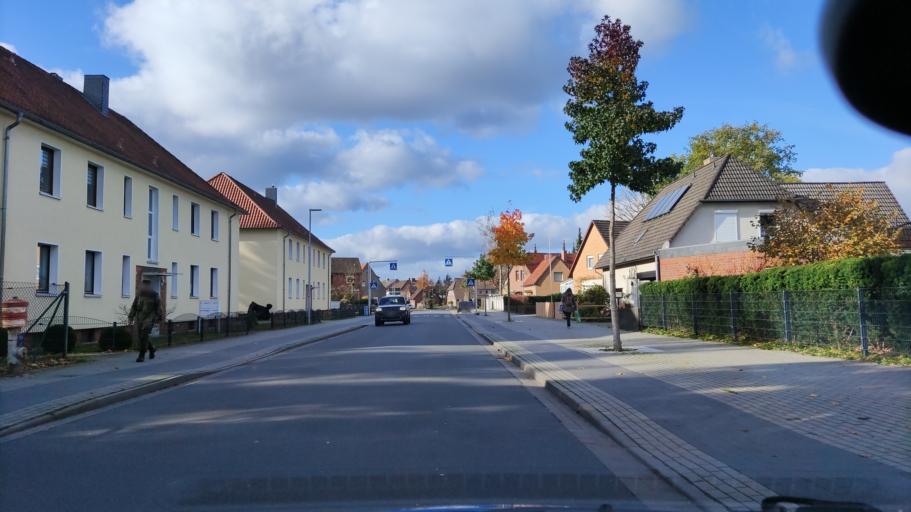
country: DE
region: Lower Saxony
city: Munster
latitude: 52.9866
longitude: 10.0990
